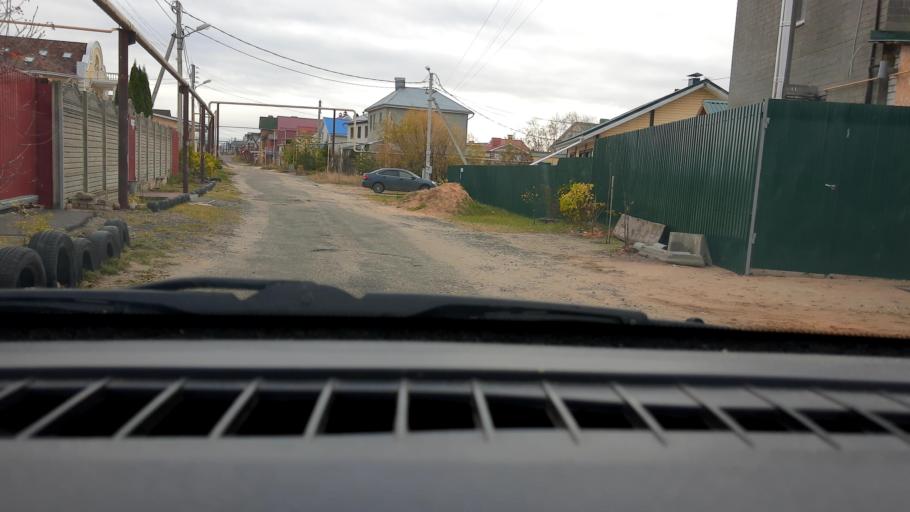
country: RU
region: Nizjnij Novgorod
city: Gorbatovka
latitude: 56.3864
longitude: 43.7624
